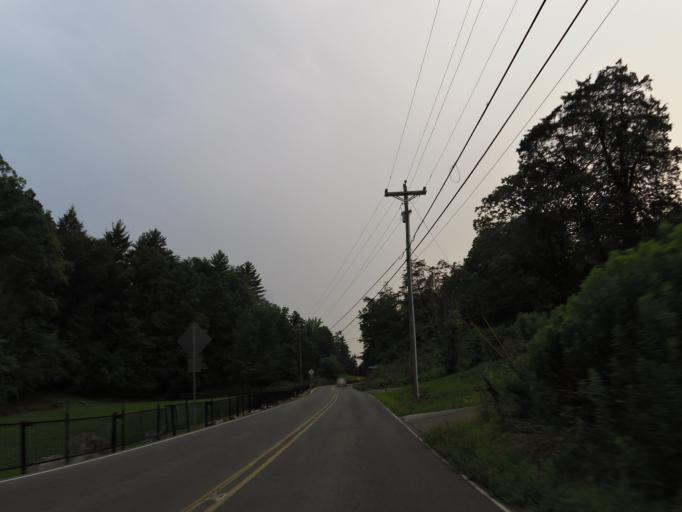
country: US
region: Tennessee
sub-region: Sevier County
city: Pigeon Forge
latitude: 35.7622
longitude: -83.6654
